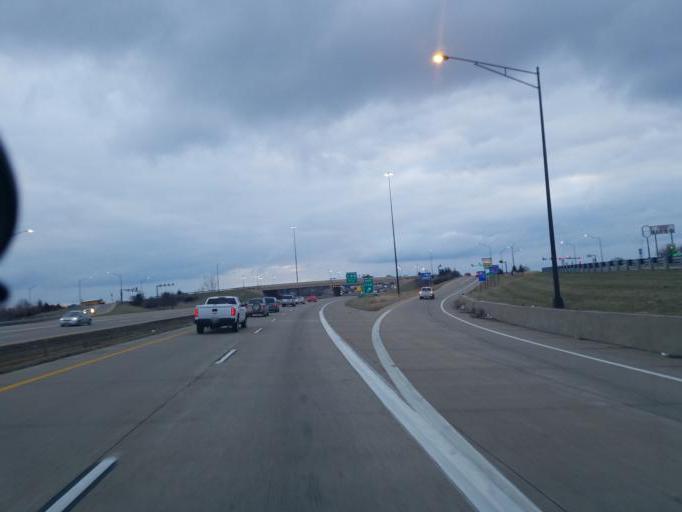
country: US
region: Missouri
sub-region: Saint Charles County
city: Wentzville
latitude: 38.8097
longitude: -90.8778
